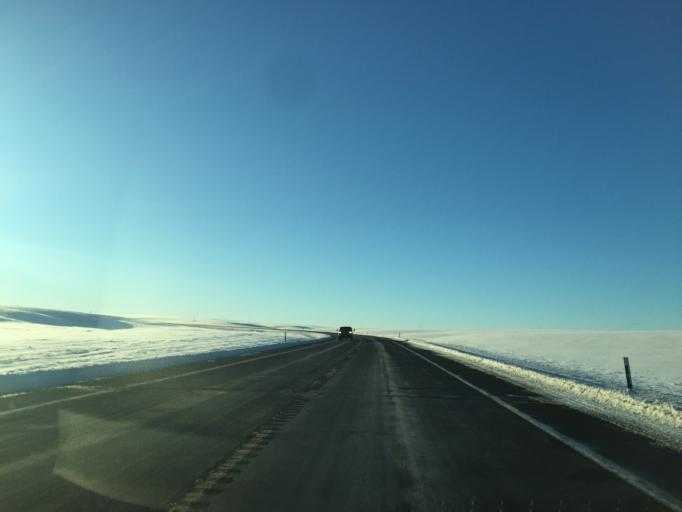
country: US
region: Washington
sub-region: Grant County
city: Soap Lake
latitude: 47.6068
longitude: -119.5010
